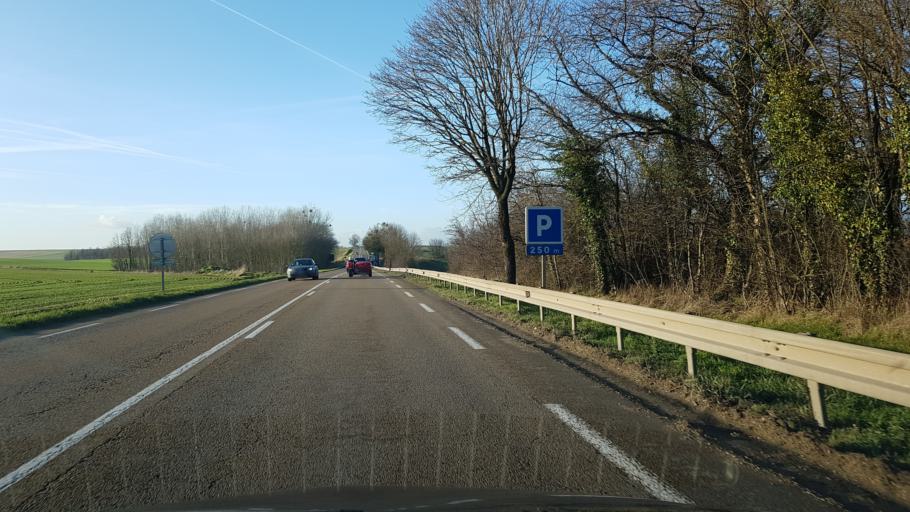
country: FR
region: Champagne-Ardenne
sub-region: Departement de la Marne
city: Vitry-le-Francois
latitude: 48.7371
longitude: 4.5477
